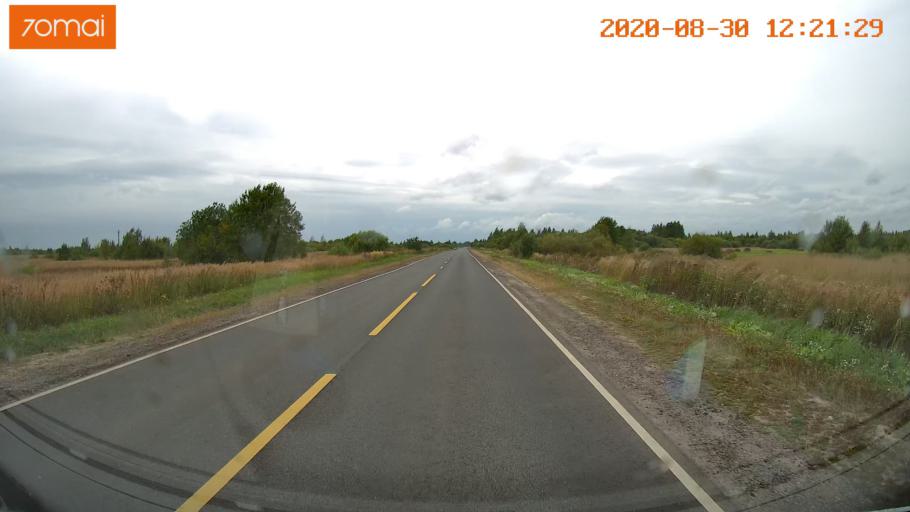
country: RU
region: Ivanovo
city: Yur'yevets
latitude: 57.3254
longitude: 42.8745
